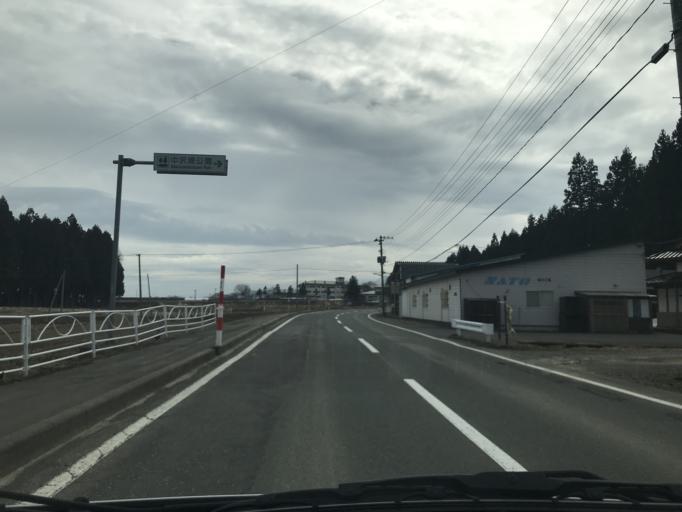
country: JP
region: Iwate
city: Hanamaki
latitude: 39.3585
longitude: 140.9904
